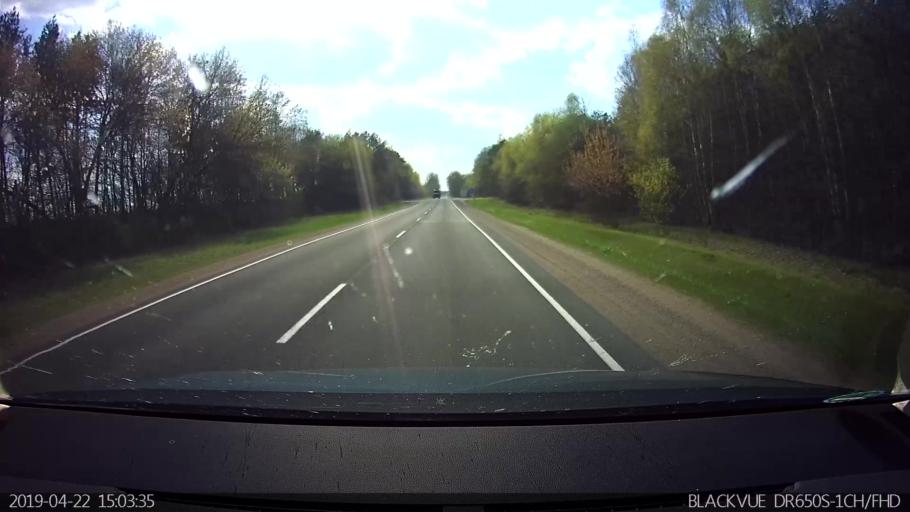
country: BY
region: Brest
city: Kamyanyets
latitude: 52.3443
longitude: 23.9179
